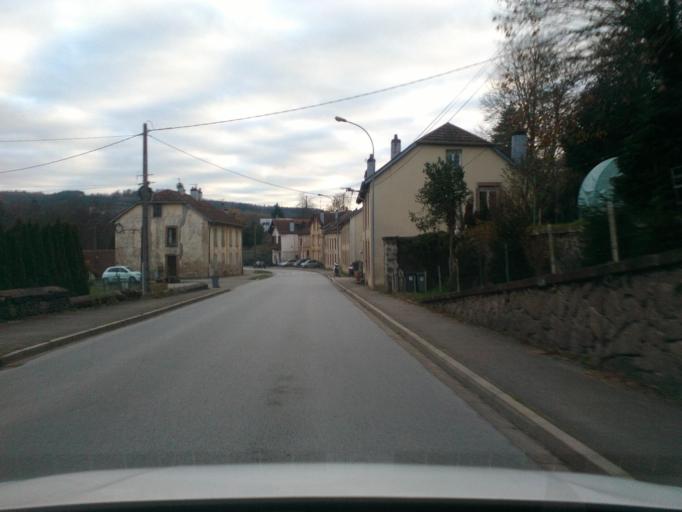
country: FR
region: Lorraine
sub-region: Departement des Vosges
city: Senones
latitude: 48.4004
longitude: 6.9858
